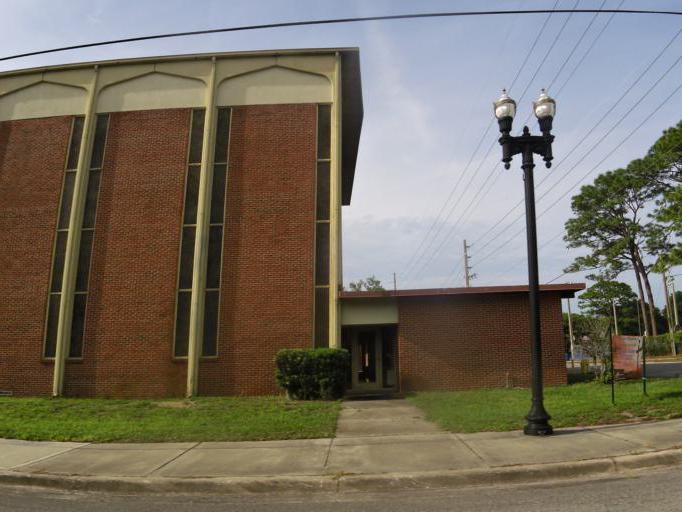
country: US
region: Florida
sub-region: Duval County
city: Jacksonville
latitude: 30.3337
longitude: -81.5916
